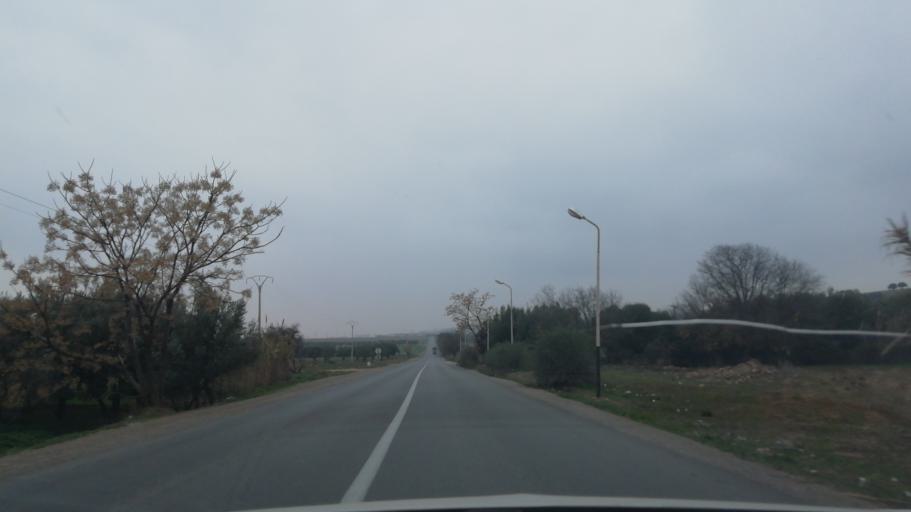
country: DZ
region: Sidi Bel Abbes
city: Sfizef
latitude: 35.2526
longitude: -0.1946
